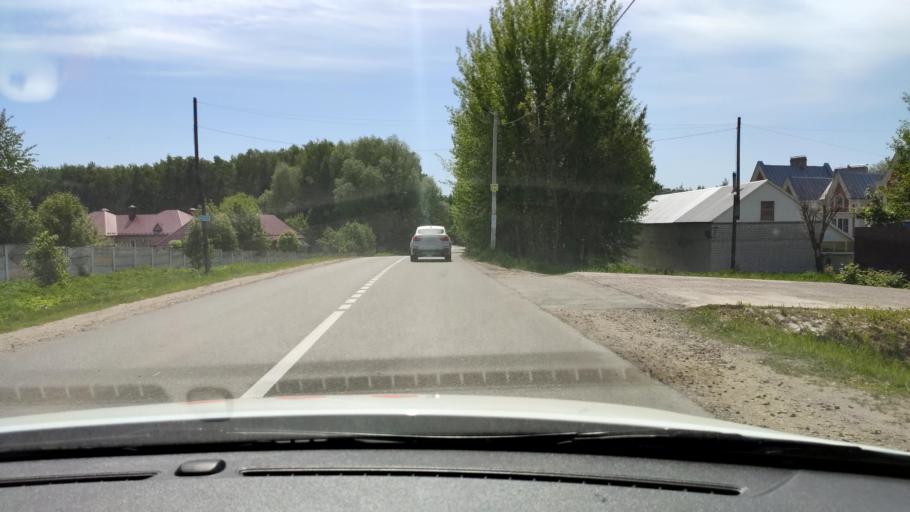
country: RU
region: Tatarstan
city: Osinovo
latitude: 55.8574
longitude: 48.8209
